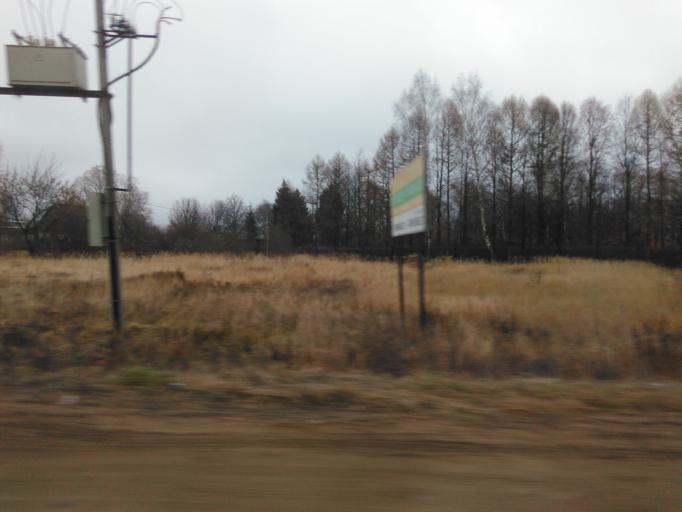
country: RU
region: Moskovskaya
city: Ashukino
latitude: 56.1707
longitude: 37.9401
